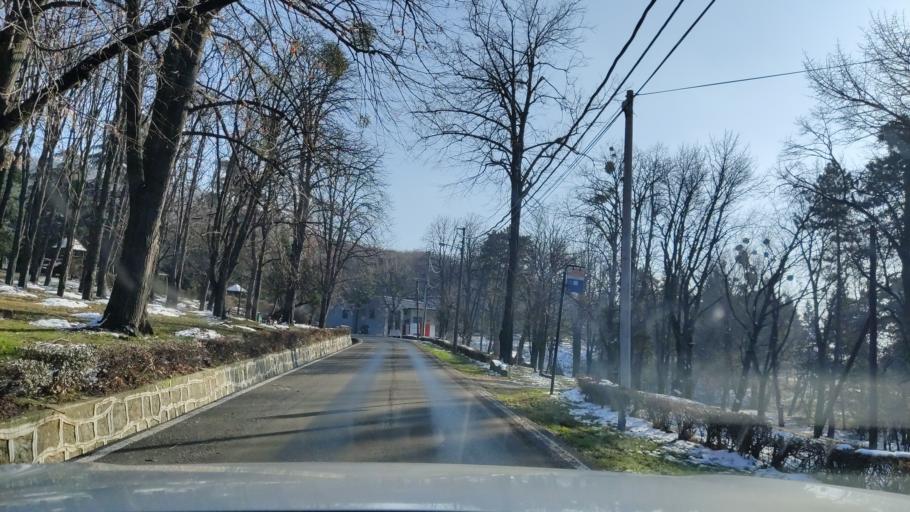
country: RS
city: Rusanj
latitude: 44.6955
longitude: 20.5022
